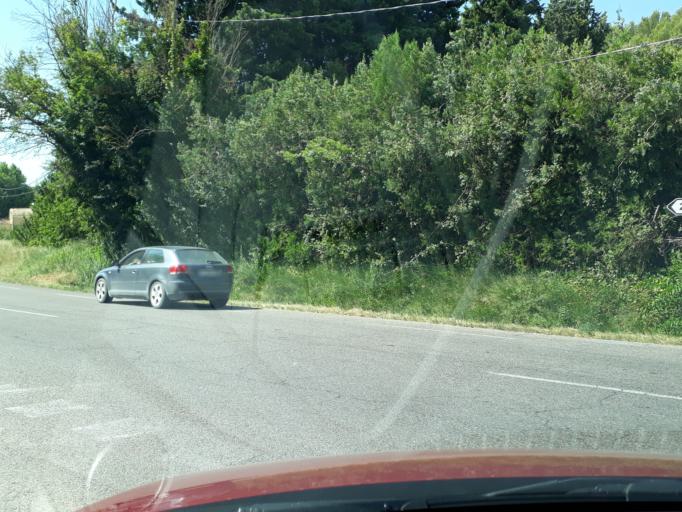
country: FR
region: Provence-Alpes-Cote d'Azur
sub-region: Departement du Vaucluse
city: Sarrians
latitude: 44.1027
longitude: 4.9837
